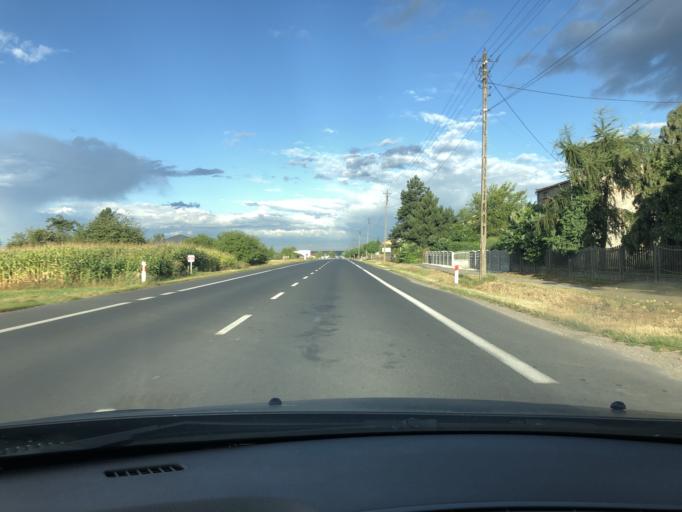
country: PL
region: Lodz Voivodeship
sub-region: Powiat wieruszowski
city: Galewice
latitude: 51.3034
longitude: 18.2773
